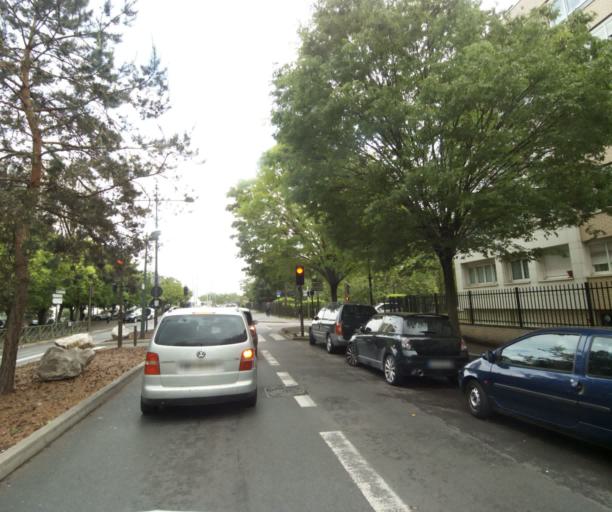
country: FR
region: Ile-de-France
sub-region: Departement du Val-d'Oise
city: Argenteuil
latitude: 48.9517
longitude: 2.2290
